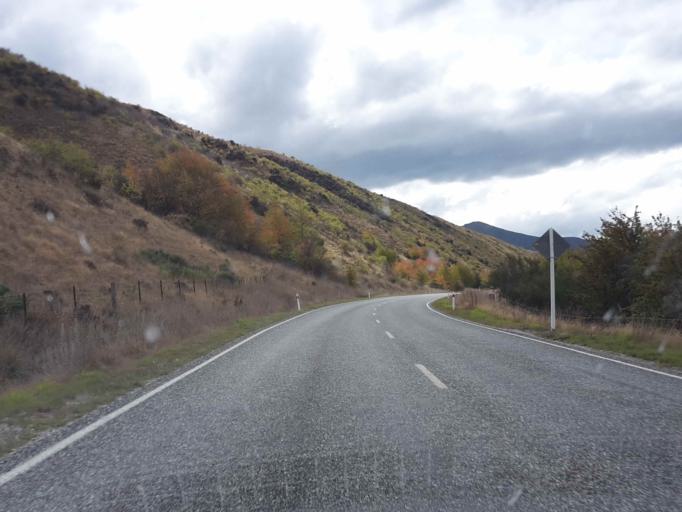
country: NZ
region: Otago
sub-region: Queenstown-Lakes District
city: Wanaka
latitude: -44.8193
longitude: 169.0625
